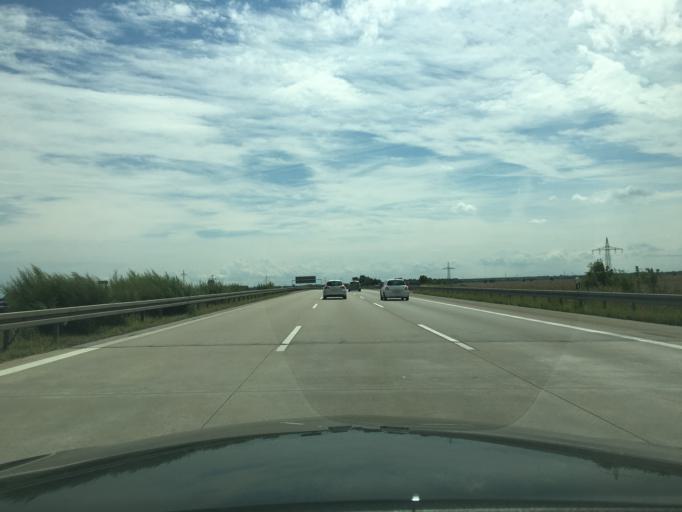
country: DE
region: Saxony-Anhalt
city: Brehna
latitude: 51.5440
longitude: 12.1921
